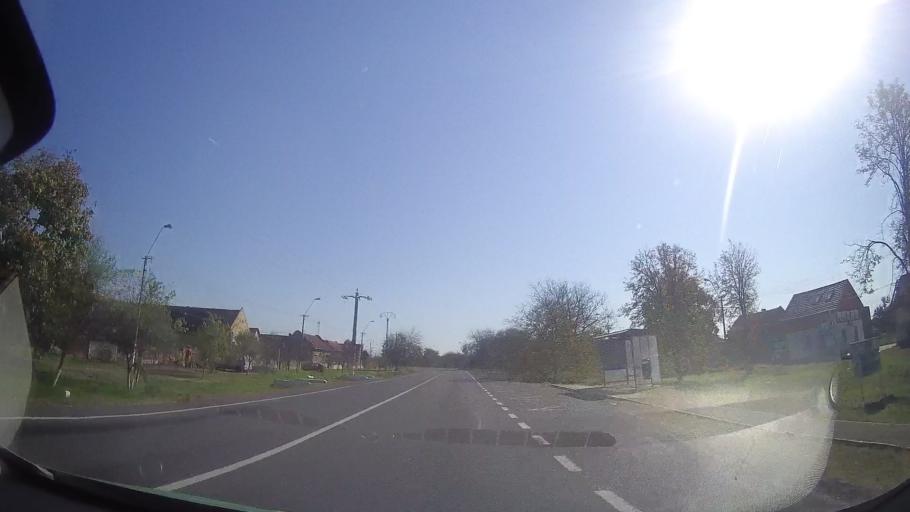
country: RO
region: Timis
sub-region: Comuna Belint
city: Belint
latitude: 45.7492
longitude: 21.7681
